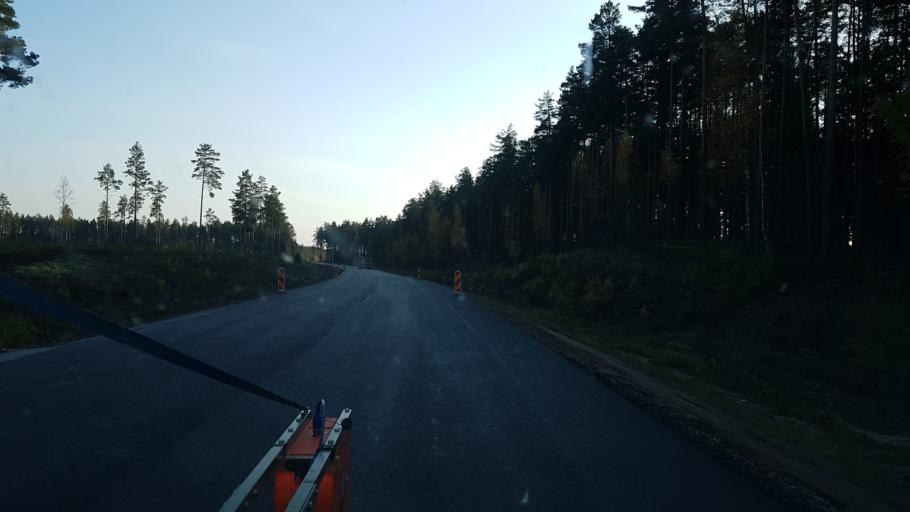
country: EE
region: Polvamaa
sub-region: Polva linn
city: Polva
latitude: 57.9287
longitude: 27.1829
